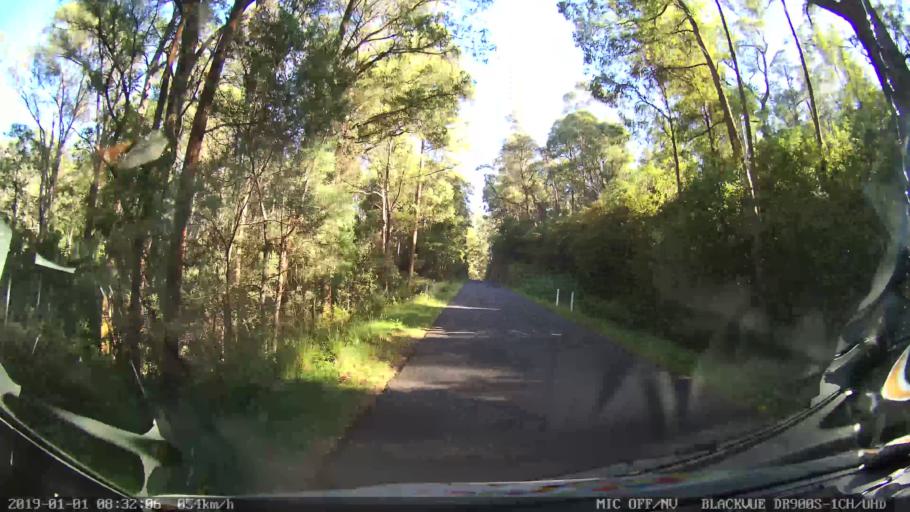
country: AU
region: New South Wales
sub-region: Snowy River
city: Jindabyne
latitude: -36.3648
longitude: 148.2057
